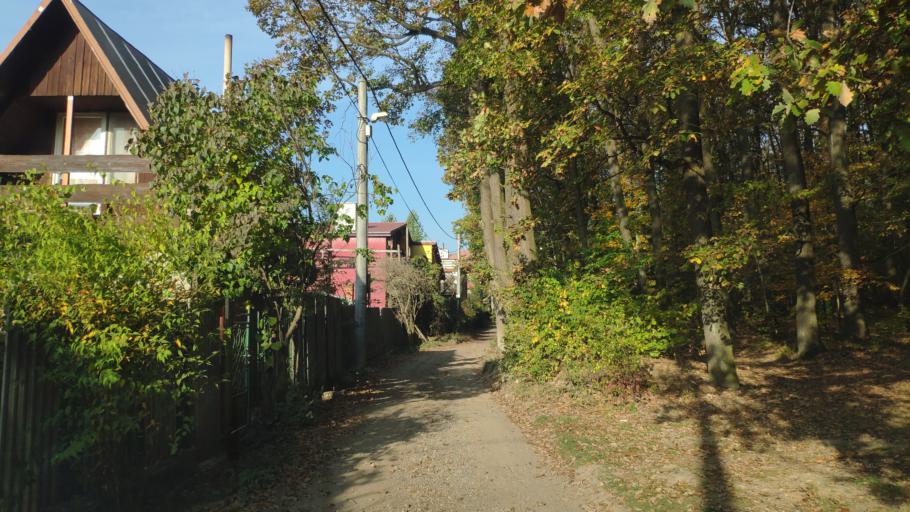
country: SK
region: Kosicky
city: Kosice
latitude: 48.7433
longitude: 21.2164
